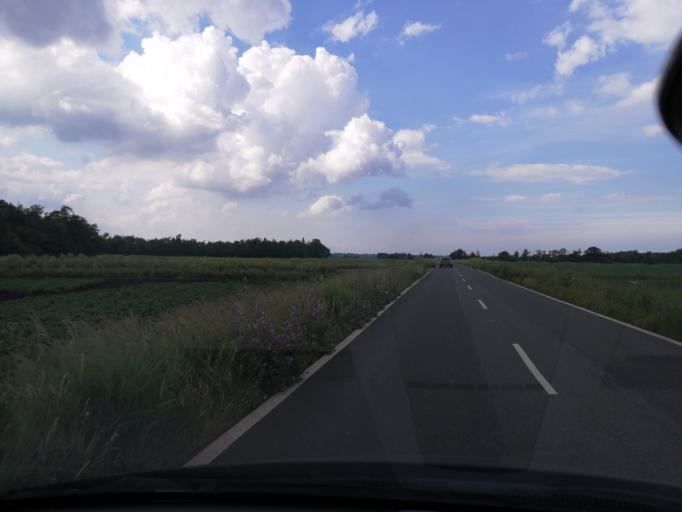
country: GB
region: England
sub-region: Cambridgeshire
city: Yaxley
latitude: 52.4840
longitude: -0.2429
